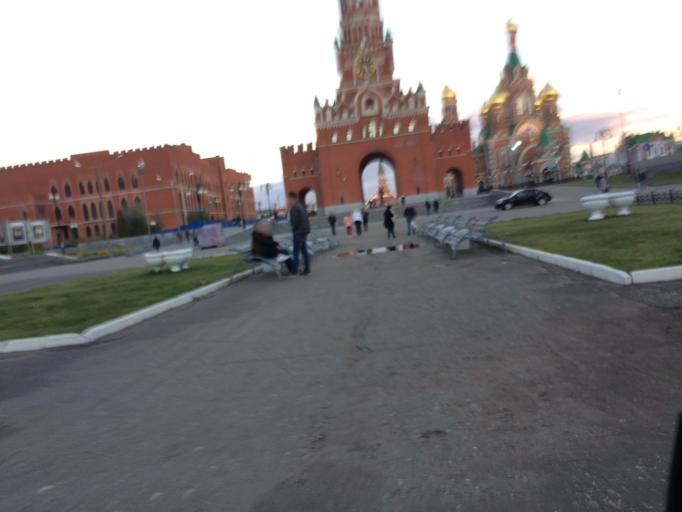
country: RU
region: Mariy-El
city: Yoshkar-Ola
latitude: 56.6341
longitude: 47.9011
